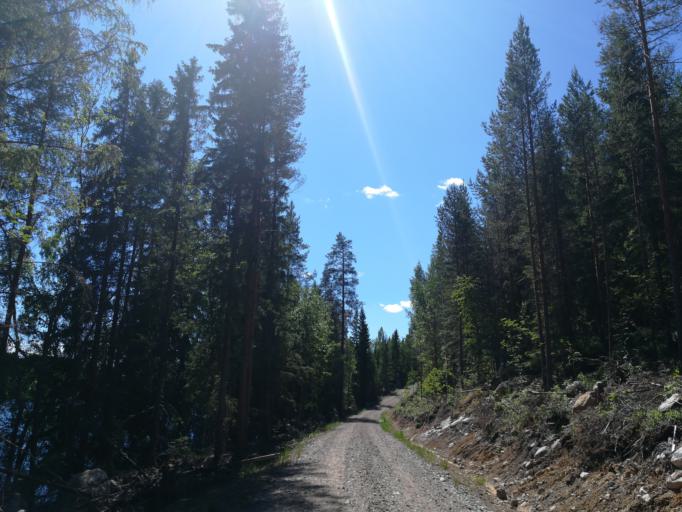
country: FI
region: Southern Savonia
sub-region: Mikkeli
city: Puumala
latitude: 61.6182
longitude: 28.1722
